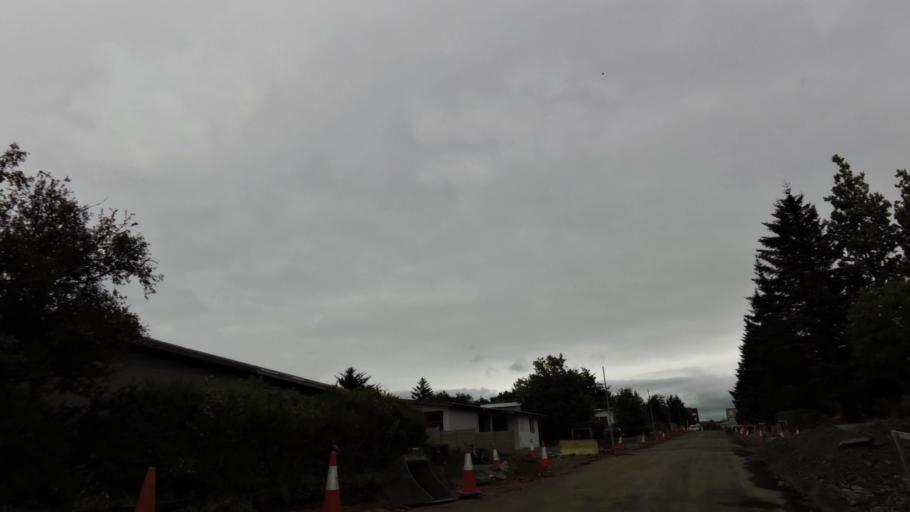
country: IS
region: Capital Region
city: Gardabaer
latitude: 64.0860
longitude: -21.9250
